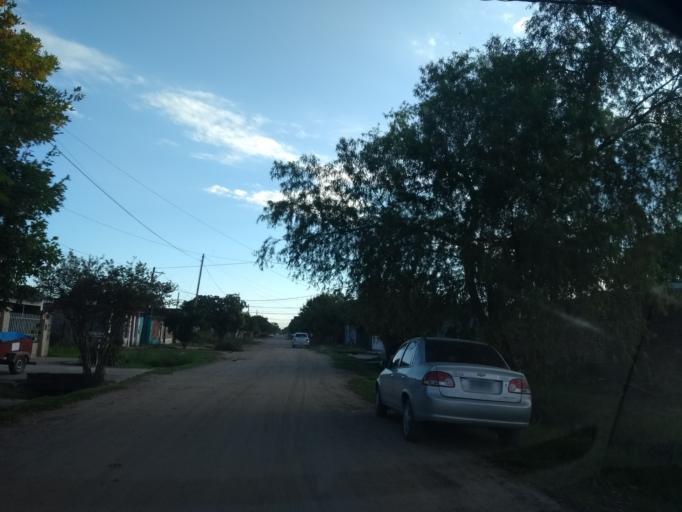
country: AR
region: Chaco
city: Barranqueras
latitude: -27.4863
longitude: -58.9417
